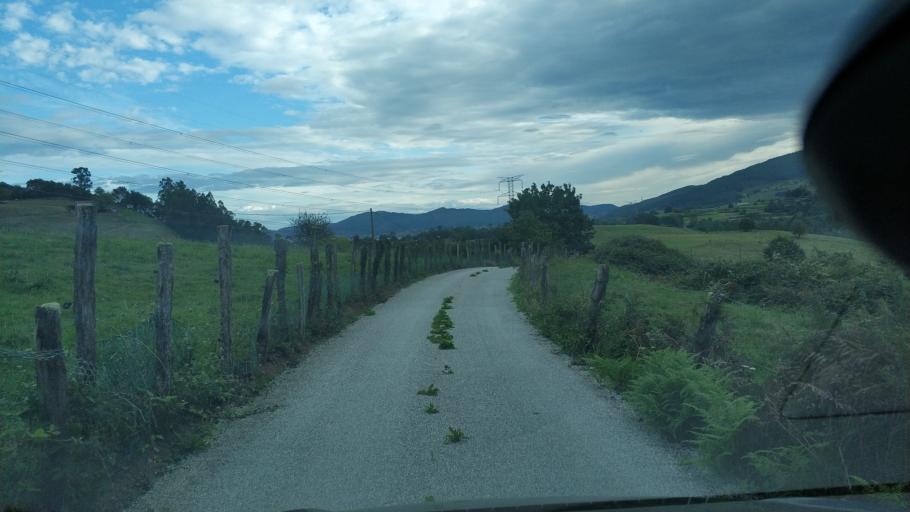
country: ES
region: Cantabria
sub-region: Provincia de Cantabria
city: Santa Maria de Cayon
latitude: 43.2917
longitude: -3.8572
